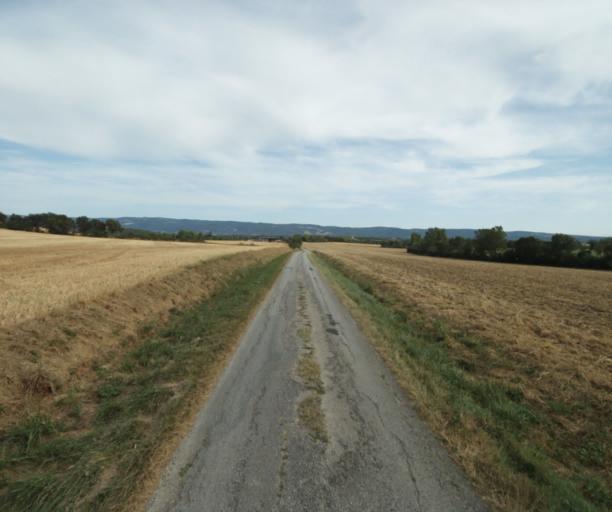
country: FR
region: Midi-Pyrenees
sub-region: Departement du Tarn
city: Puylaurens
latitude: 43.5316
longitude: 2.0354
